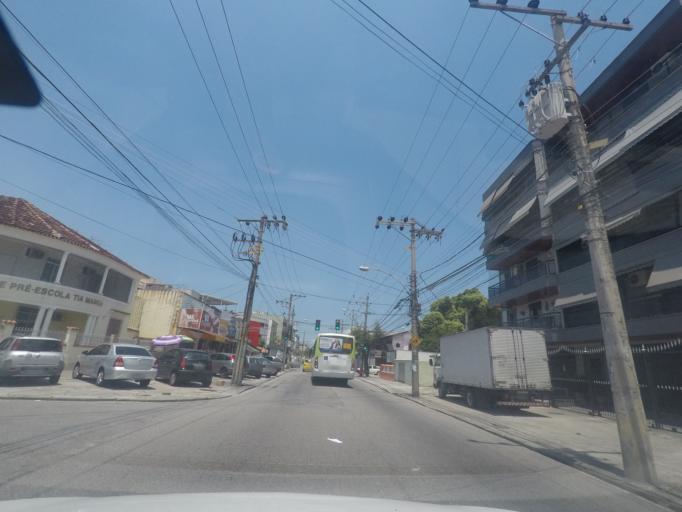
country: BR
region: Rio de Janeiro
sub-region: Duque De Caxias
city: Duque de Caxias
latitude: -22.8406
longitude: -43.3023
